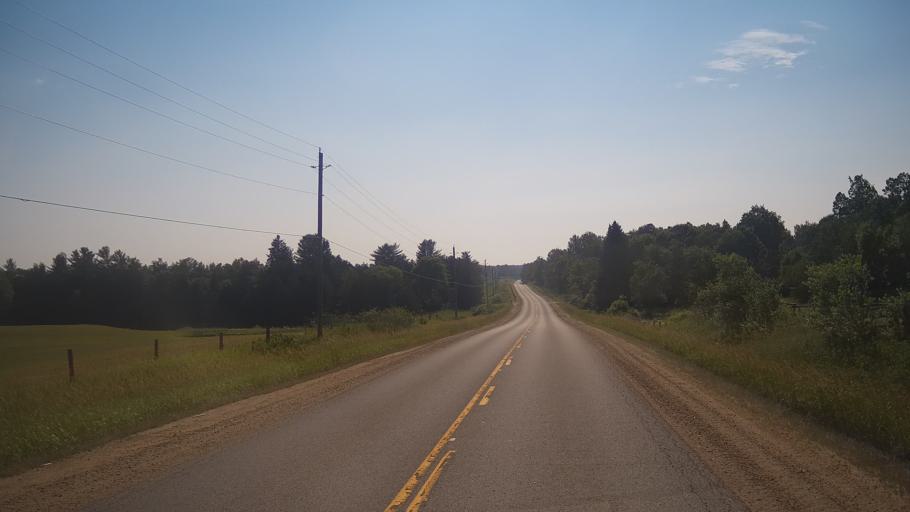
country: CA
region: Ontario
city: Pembroke
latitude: 45.6122
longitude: -77.1968
